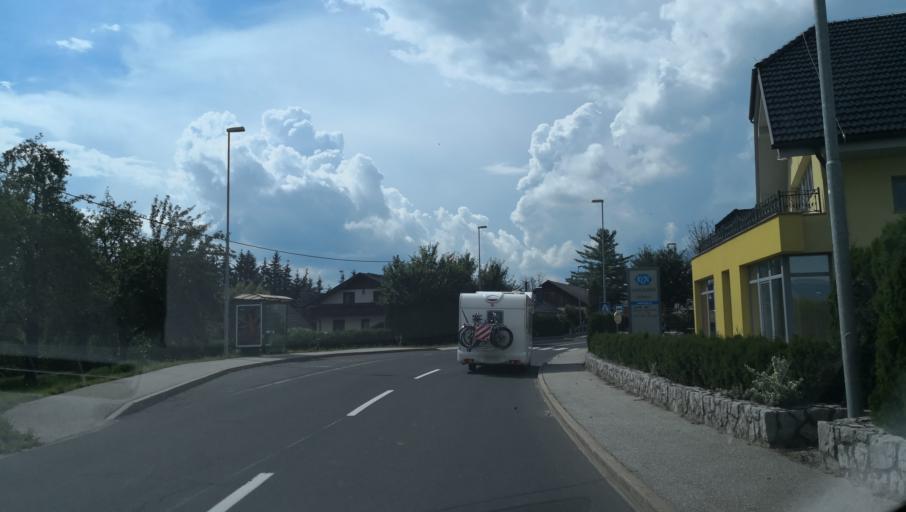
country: SI
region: Zuzemberk
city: Zuzemberk
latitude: 45.8360
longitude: 14.9207
